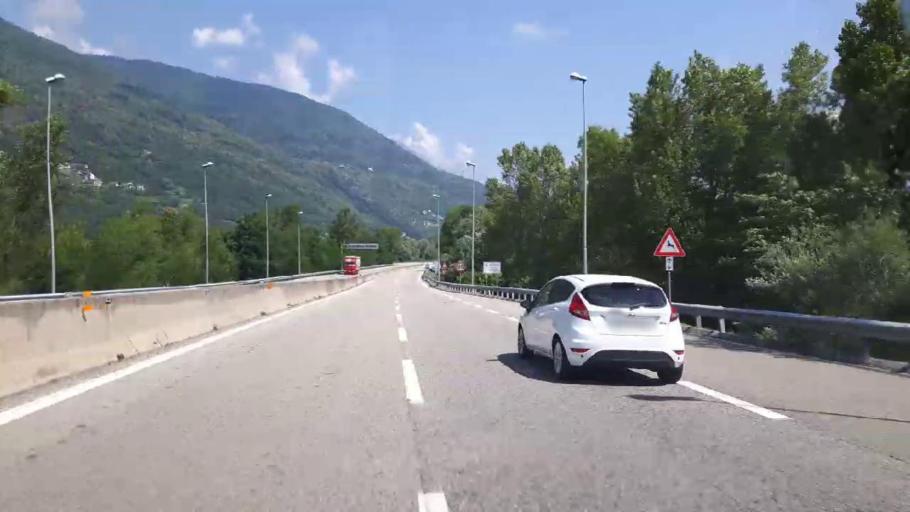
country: IT
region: Piedmont
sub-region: Provincia Verbano-Cusio-Ossola
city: Villadossola
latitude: 46.0734
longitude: 8.2774
